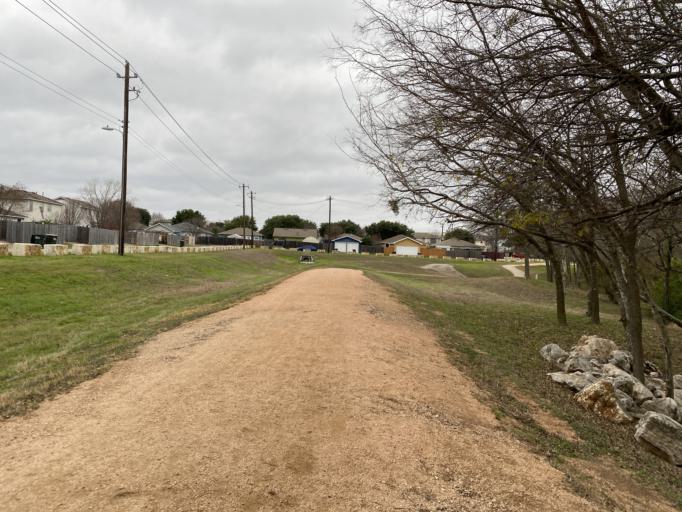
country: US
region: Texas
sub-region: Travis County
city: Wells Branch
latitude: 30.4216
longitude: -97.6569
